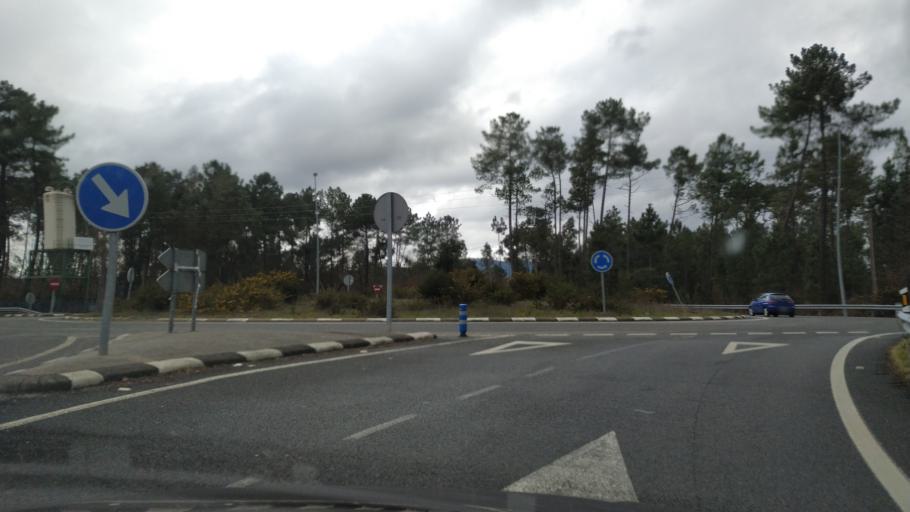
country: ES
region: Galicia
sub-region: Provincia de Ourense
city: Maside
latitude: 42.4526
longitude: -8.0276
